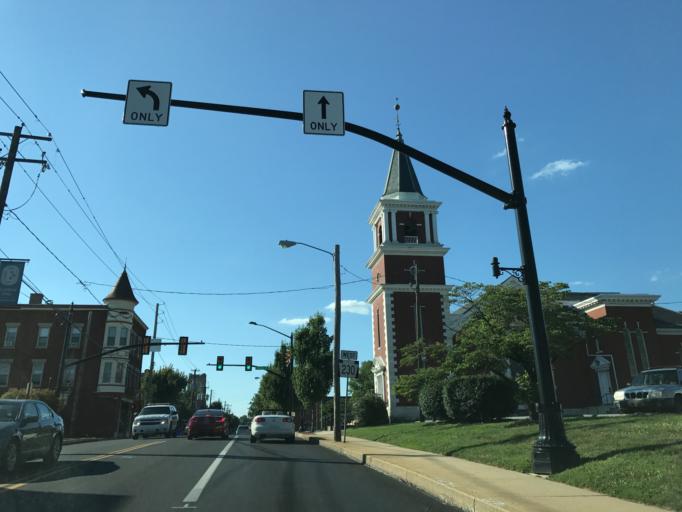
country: US
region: Pennsylvania
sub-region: Lancaster County
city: Elizabethtown
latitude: 40.1476
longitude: -76.6034
